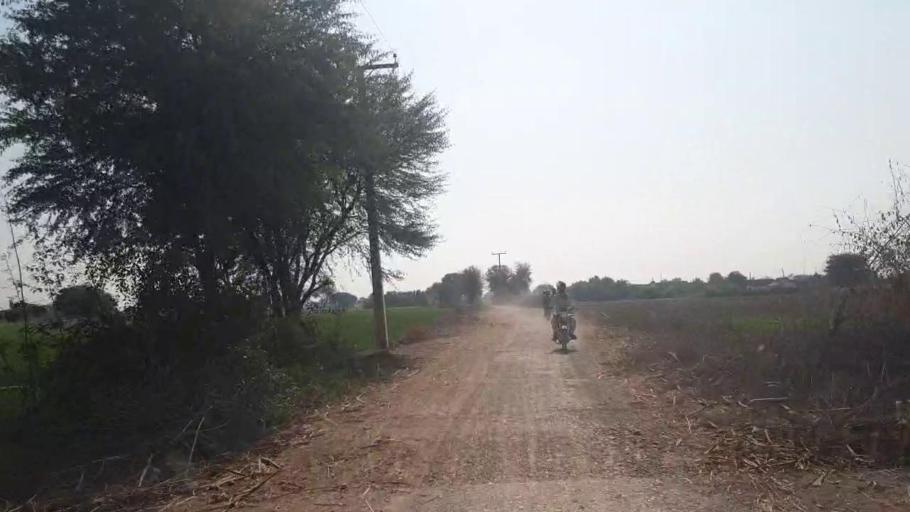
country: PK
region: Sindh
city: Shahdadpur
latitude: 26.0429
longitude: 68.4626
